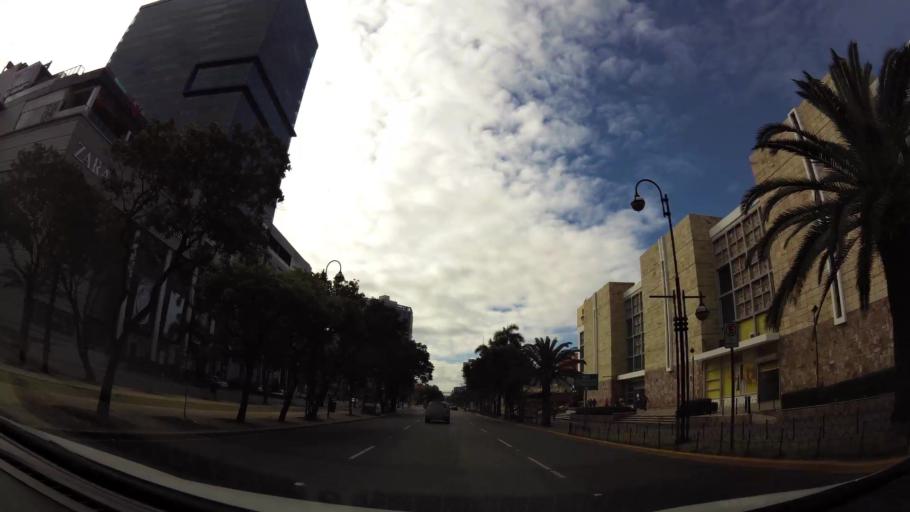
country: DO
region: Nacional
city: La Julia
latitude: 18.4731
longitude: -69.9420
